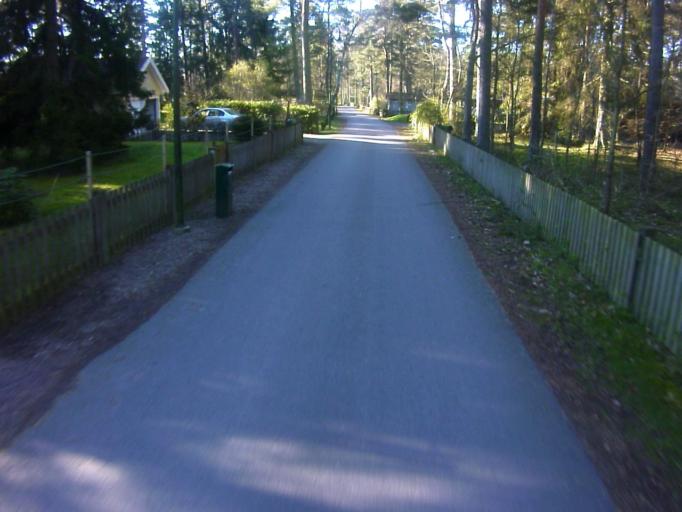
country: SE
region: Skane
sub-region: Kavlinge Kommun
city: Hofterup
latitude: 55.8138
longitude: 12.9727
